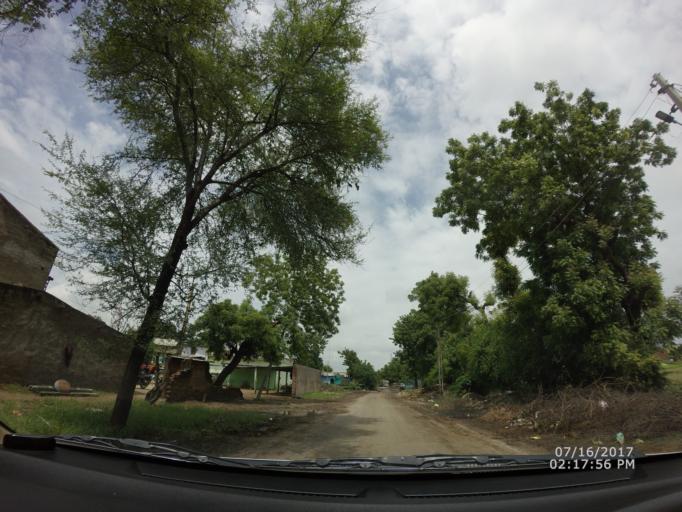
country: IN
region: Gujarat
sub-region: Mahesana
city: Kadi
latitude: 23.1417
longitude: 72.2700
